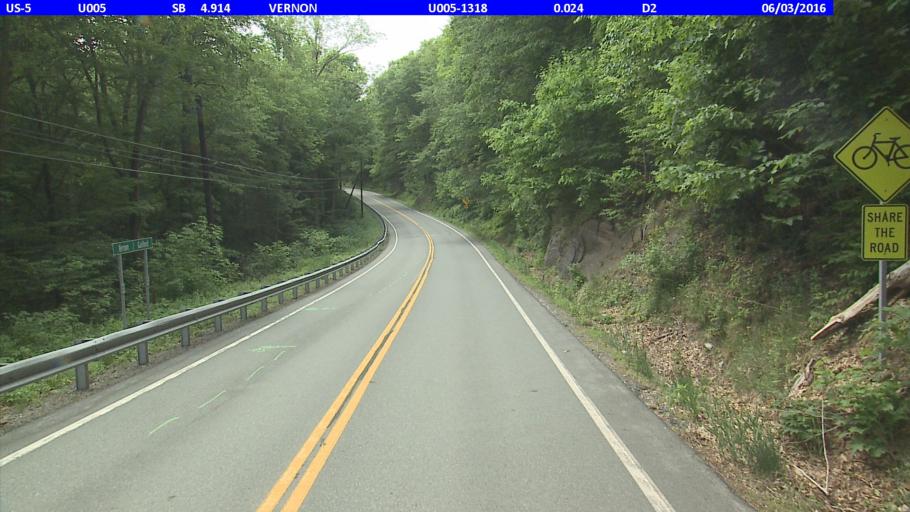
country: US
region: Vermont
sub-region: Windham County
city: Brattleboro
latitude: 42.7983
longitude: -72.5631
